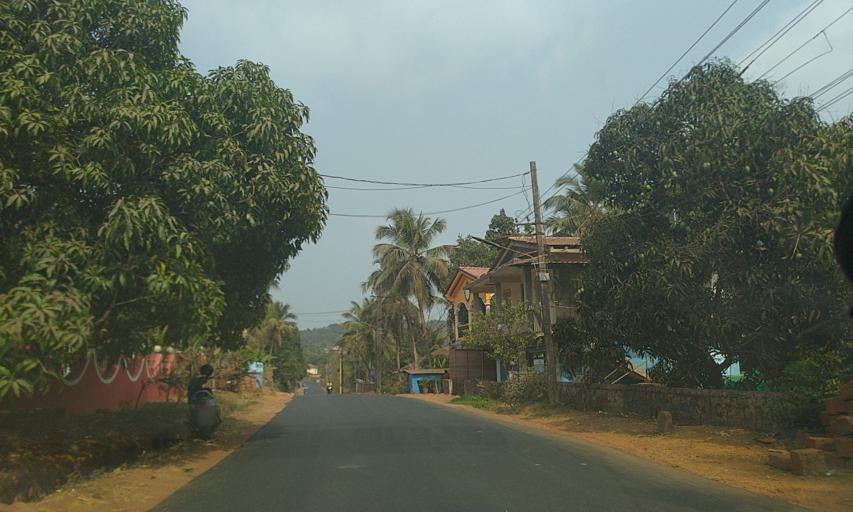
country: IN
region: Goa
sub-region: South Goa
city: Raia
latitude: 15.3072
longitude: 73.9705
